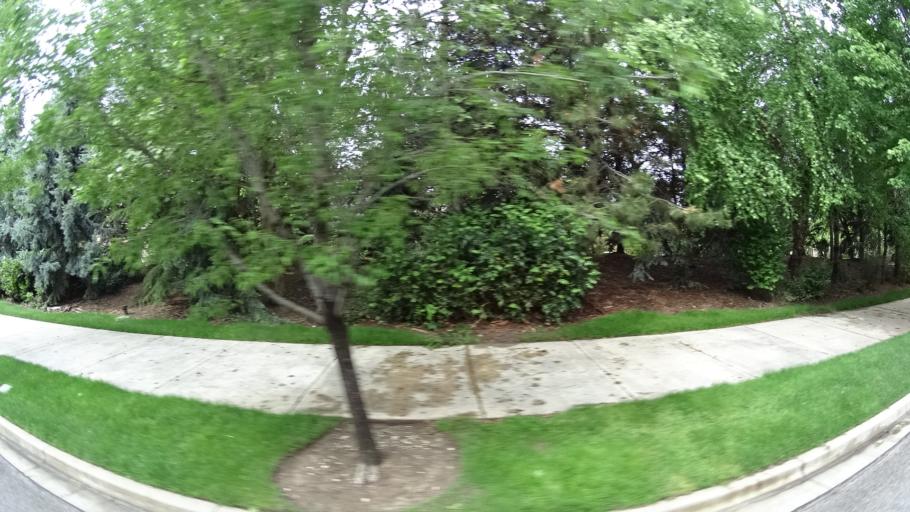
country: US
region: Idaho
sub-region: Ada County
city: Eagle
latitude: 43.6781
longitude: -116.3563
